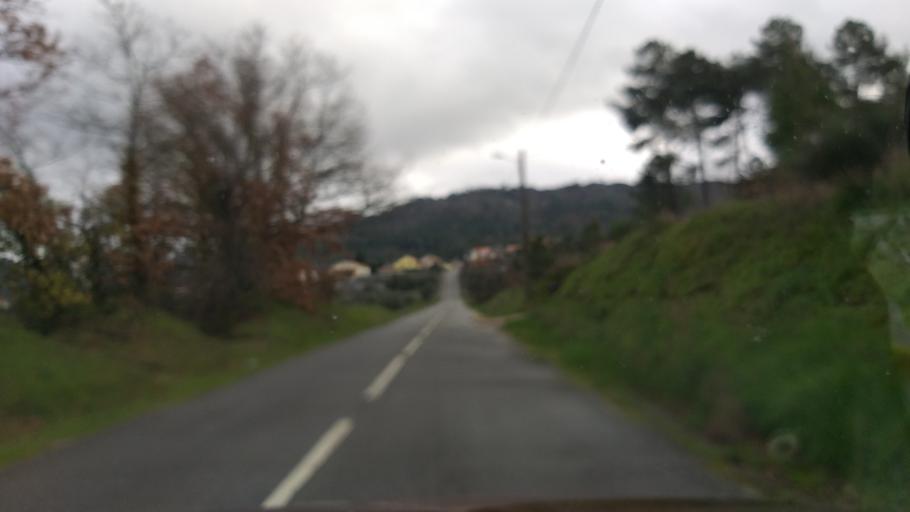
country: PT
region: Guarda
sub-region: Celorico da Beira
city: Celorico da Beira
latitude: 40.7079
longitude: -7.4377
